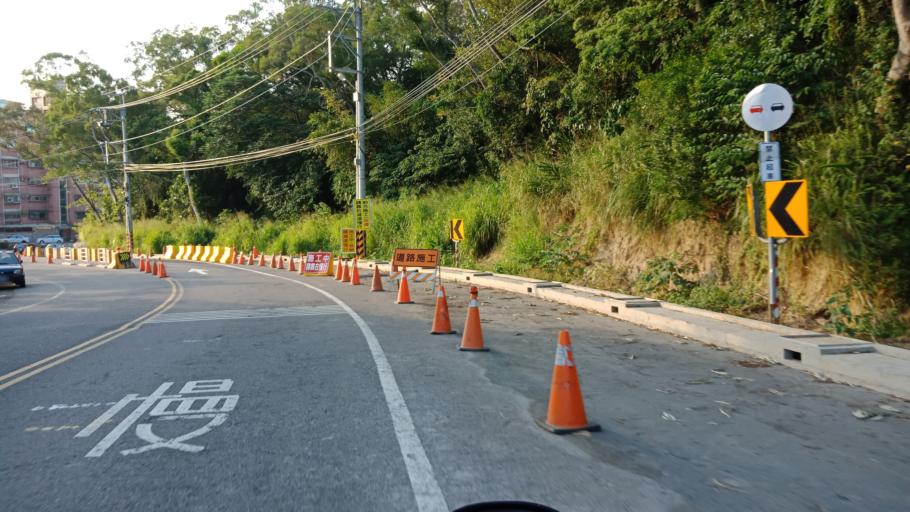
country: TW
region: Taiwan
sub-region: Hsinchu
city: Hsinchu
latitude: 24.7628
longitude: 120.9926
